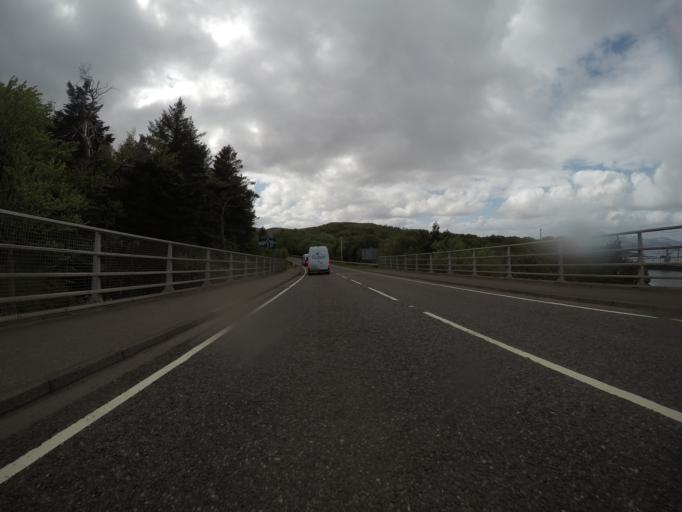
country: GB
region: Scotland
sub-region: Highland
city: Portree
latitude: 57.2743
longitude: -5.7445
